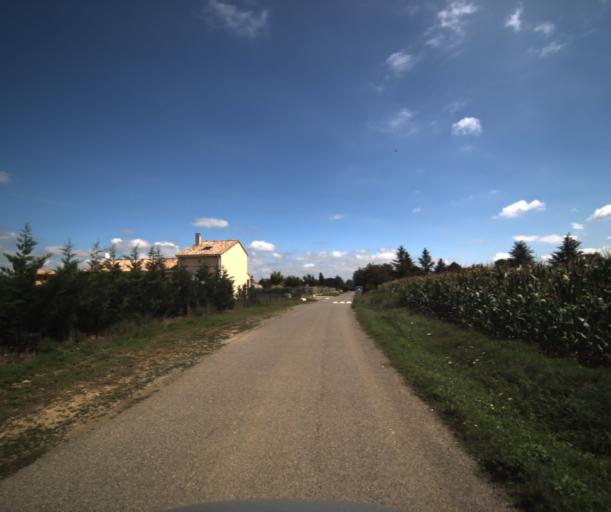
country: FR
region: Midi-Pyrenees
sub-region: Departement de la Haute-Garonne
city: Lacasse
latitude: 43.3874
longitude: 1.2595
